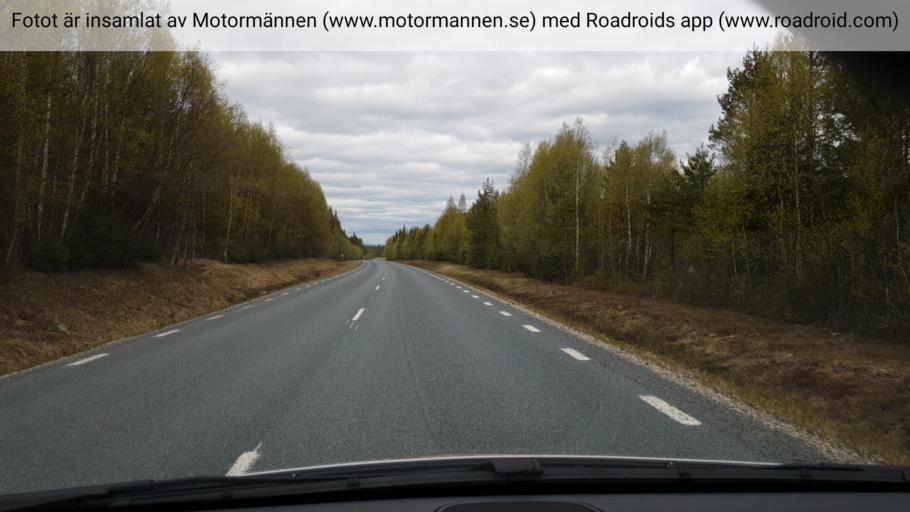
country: SE
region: Vaesterbotten
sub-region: Lycksele Kommun
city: Soderfors
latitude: 65.2115
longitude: 18.2034
